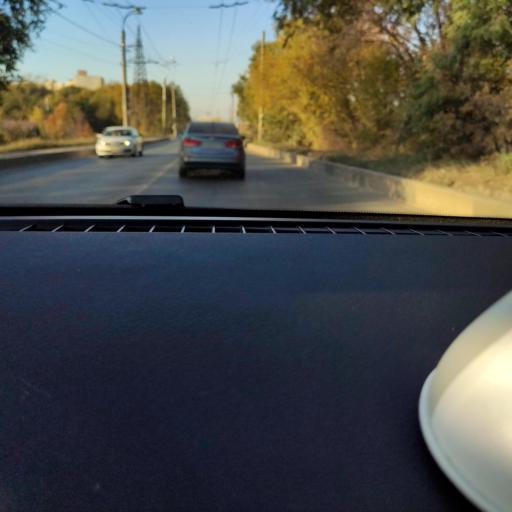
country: RU
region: Samara
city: Samara
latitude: 53.1526
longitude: 50.0921
